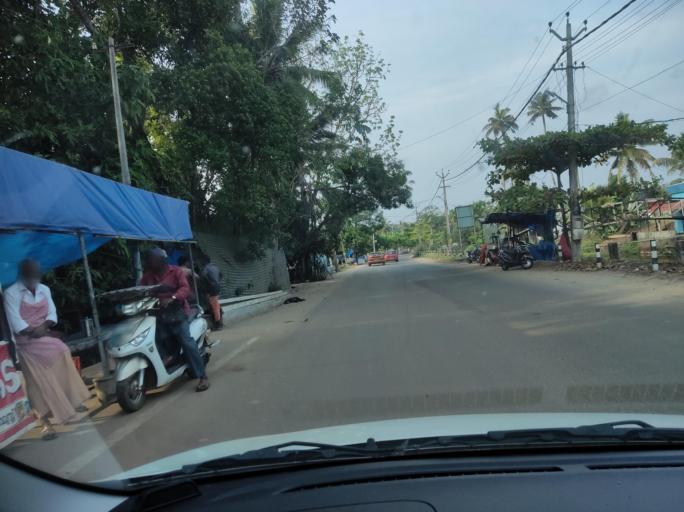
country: IN
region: Kerala
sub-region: Kottayam
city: Kottayam
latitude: 9.5751
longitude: 76.5002
